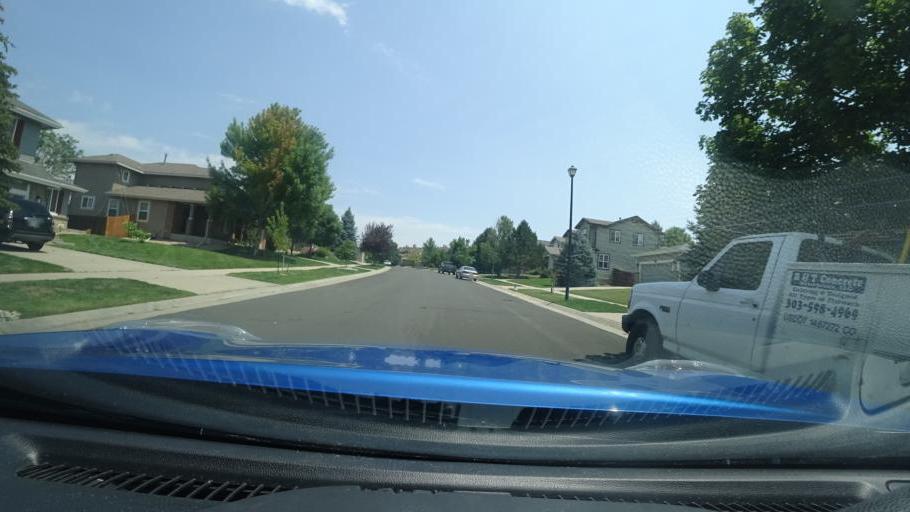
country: US
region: Colorado
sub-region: Adams County
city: Aurora
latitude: 39.6715
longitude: -104.7609
